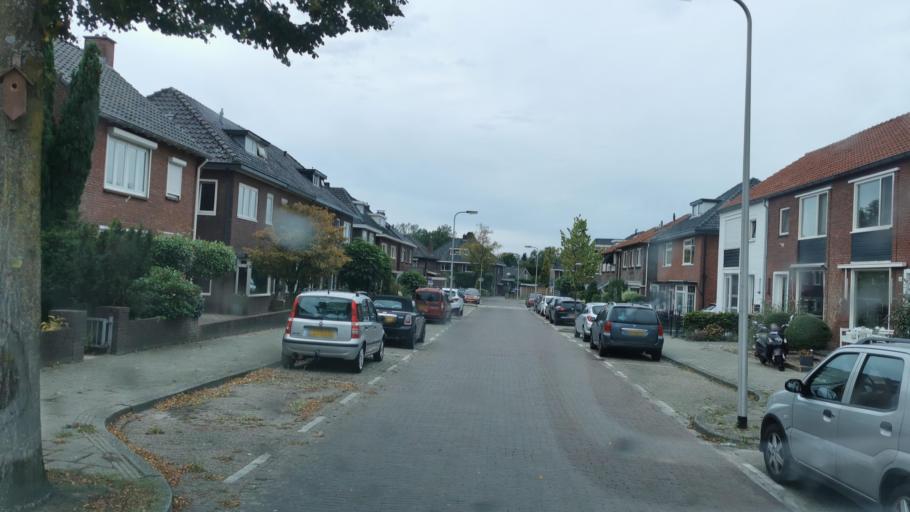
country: NL
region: Overijssel
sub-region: Gemeente Enschede
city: Enschede
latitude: 52.2313
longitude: 6.9150
